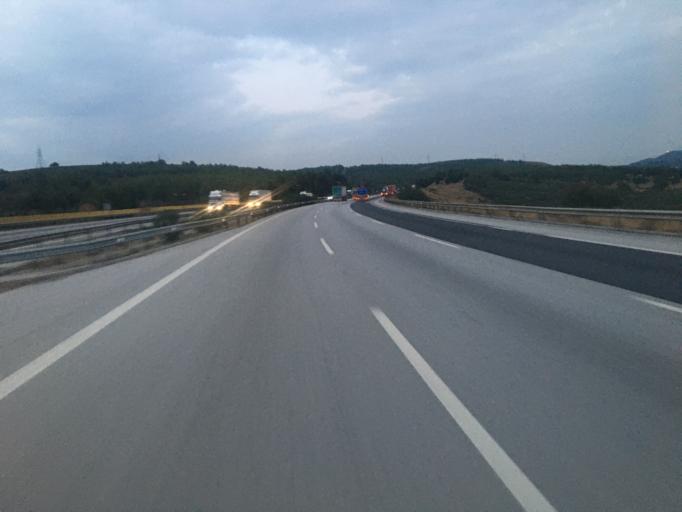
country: TR
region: Osmaniye
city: Haruniye
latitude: 37.1721
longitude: 36.3659
